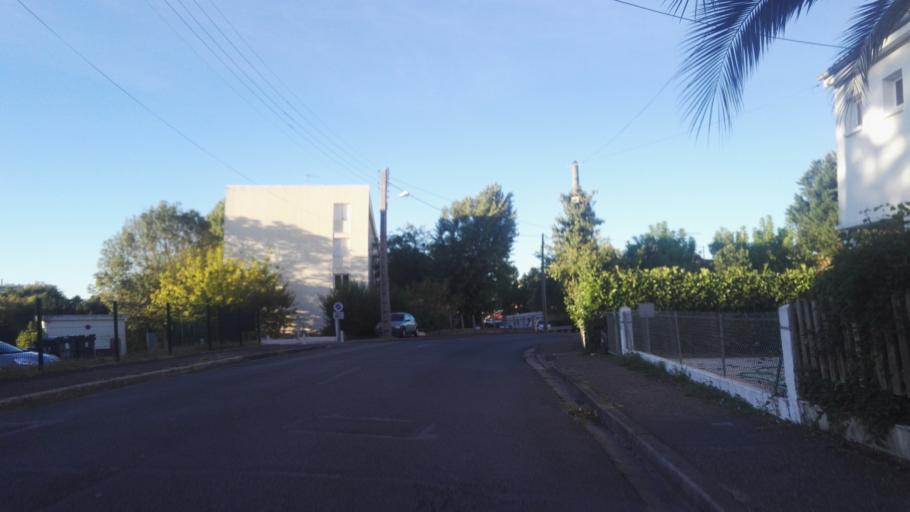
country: FR
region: Aquitaine
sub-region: Departement de la Gironde
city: Talence
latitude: 44.8057
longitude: -0.5802
